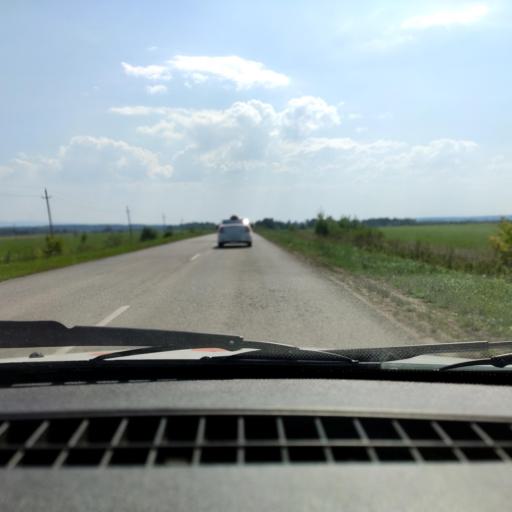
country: RU
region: Bashkortostan
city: Kudeyevskiy
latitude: 54.8408
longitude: 56.7949
